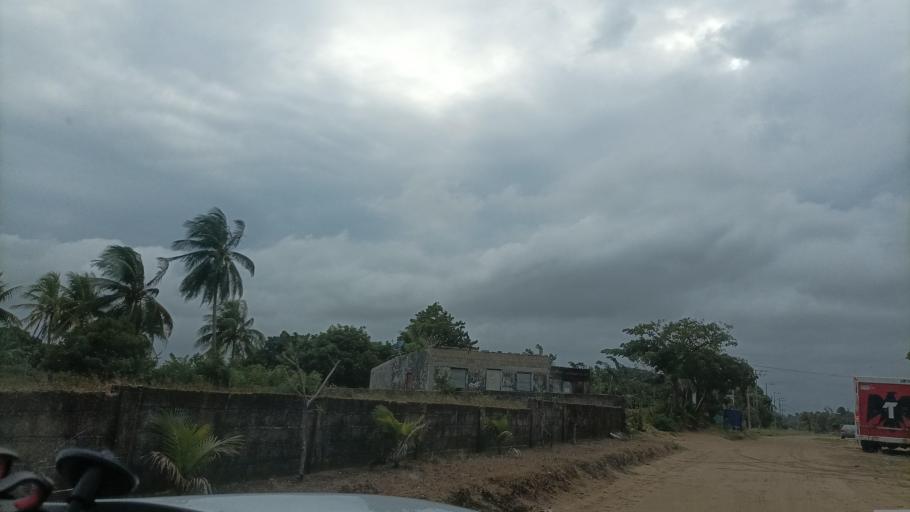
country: MX
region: Veracruz
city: Agua Dulce
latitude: 18.2061
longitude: -94.1449
